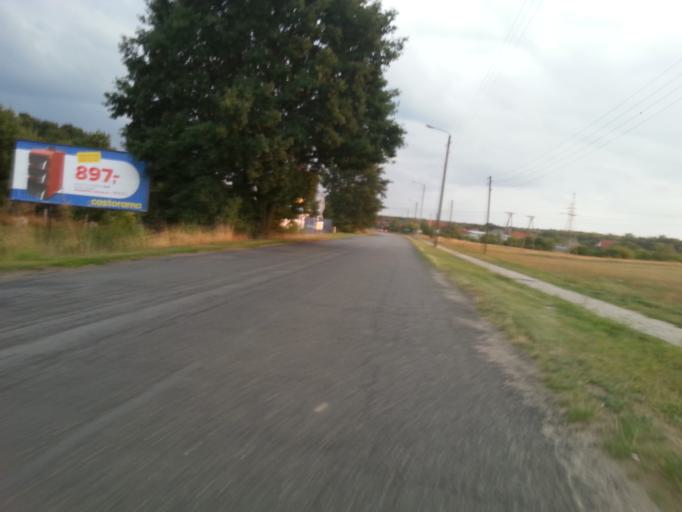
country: PL
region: Lower Silesian Voivodeship
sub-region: Powiat olesnicki
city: Twardogora
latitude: 51.3581
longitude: 17.4554
